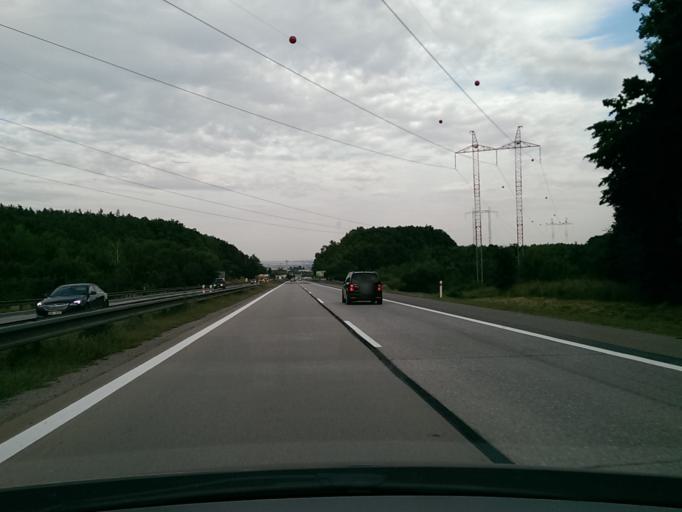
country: CZ
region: South Moravian
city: Troubsko
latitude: 49.1848
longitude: 16.4675
